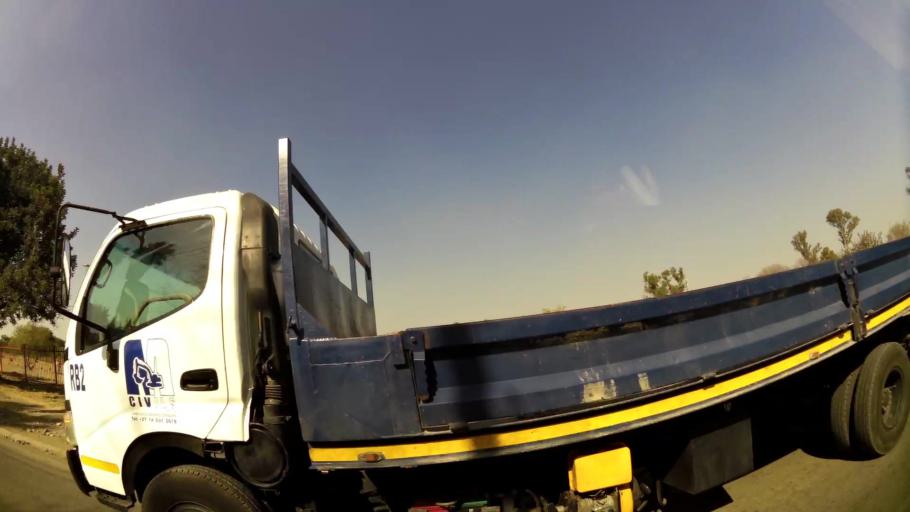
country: ZA
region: North-West
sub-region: Bojanala Platinum District Municipality
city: Rustenburg
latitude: -25.6577
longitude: 27.2376
